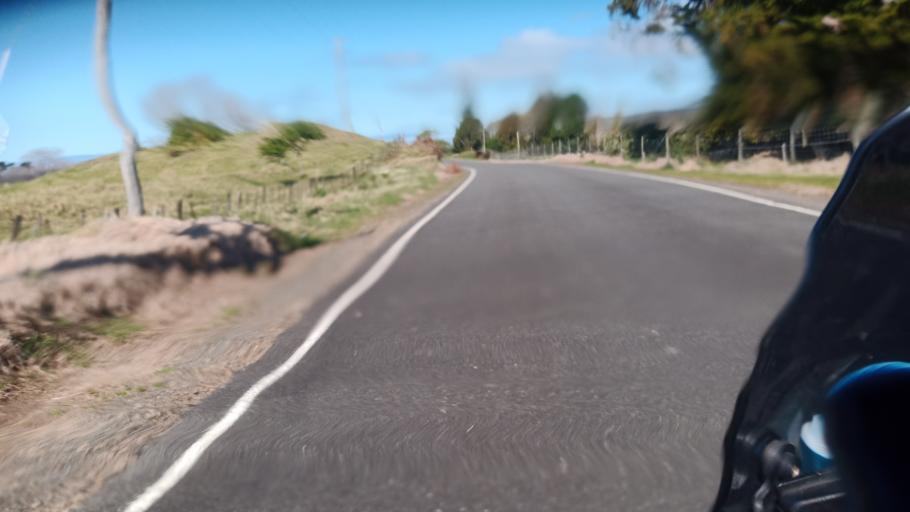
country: NZ
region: Gisborne
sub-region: Gisborne District
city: Gisborne
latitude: -39.0444
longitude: 177.8601
